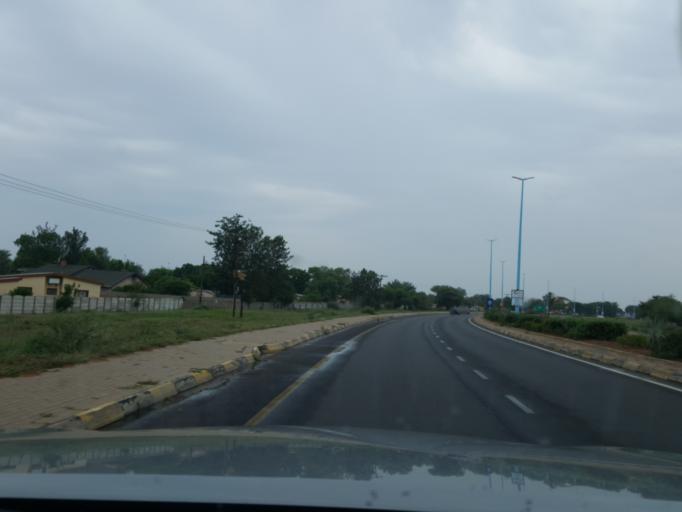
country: BW
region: South East
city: Gaborone
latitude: -24.6180
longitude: 25.9312
